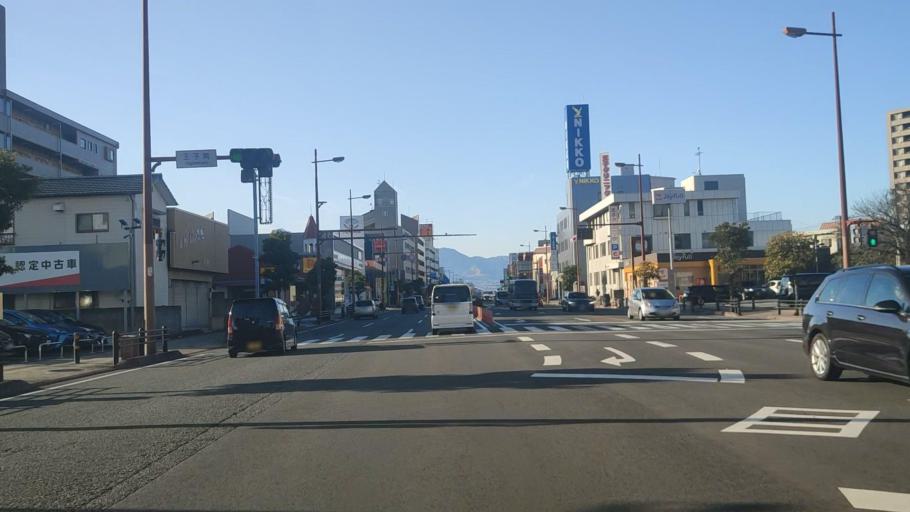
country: JP
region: Oita
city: Oita
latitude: 33.2419
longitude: 131.5918
